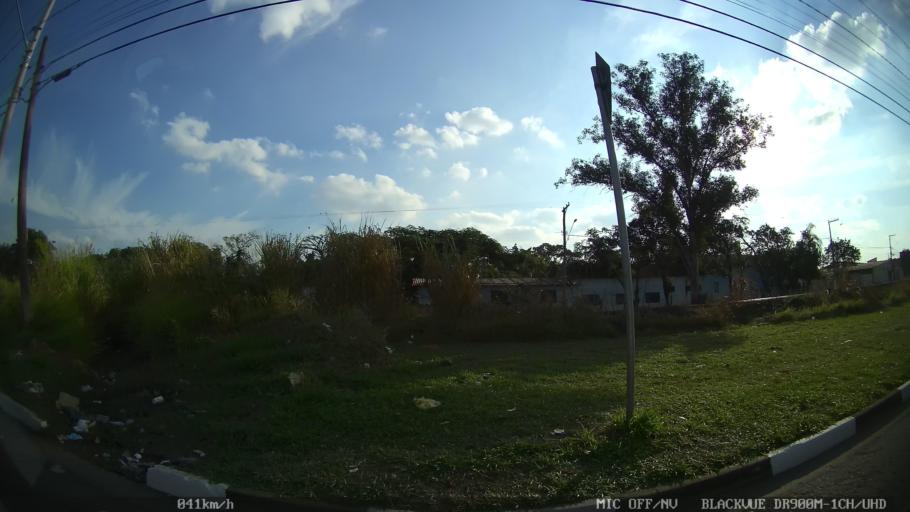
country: BR
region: Sao Paulo
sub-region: Hortolandia
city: Hortolandia
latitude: -22.8705
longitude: -47.1561
